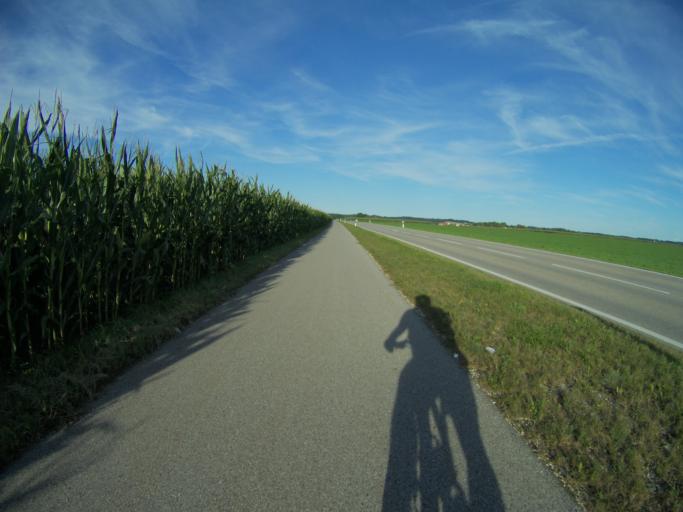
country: DE
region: Bavaria
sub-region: Upper Bavaria
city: Berglern
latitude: 48.3897
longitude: 11.9566
